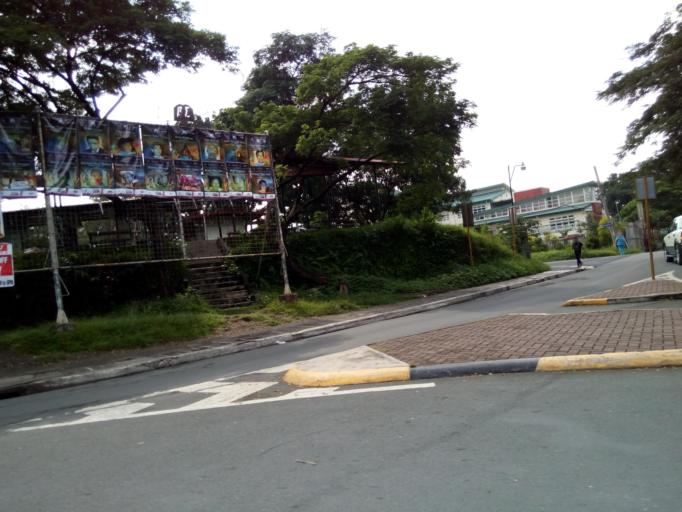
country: PH
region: Metro Manila
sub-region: Quezon City
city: Quezon City
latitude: 14.6535
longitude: 121.0726
